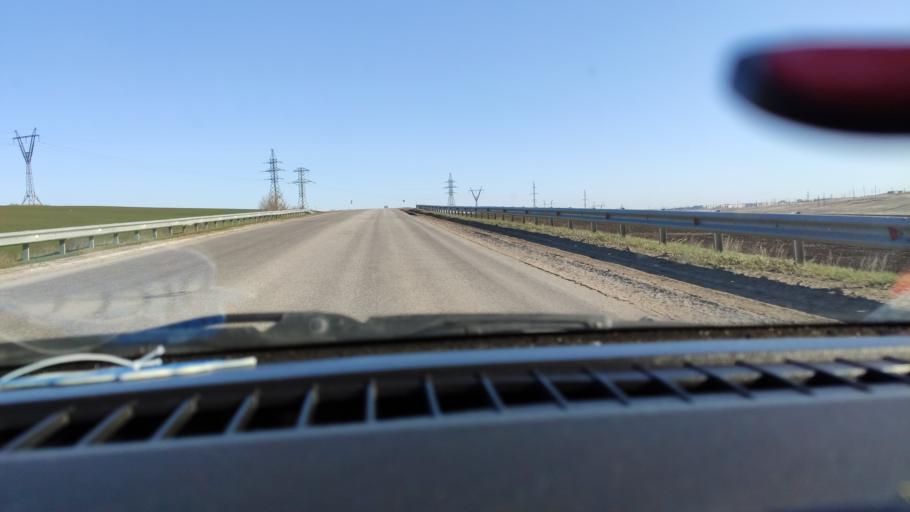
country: RU
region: Samara
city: Varlamovo
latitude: 53.0790
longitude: 48.3543
